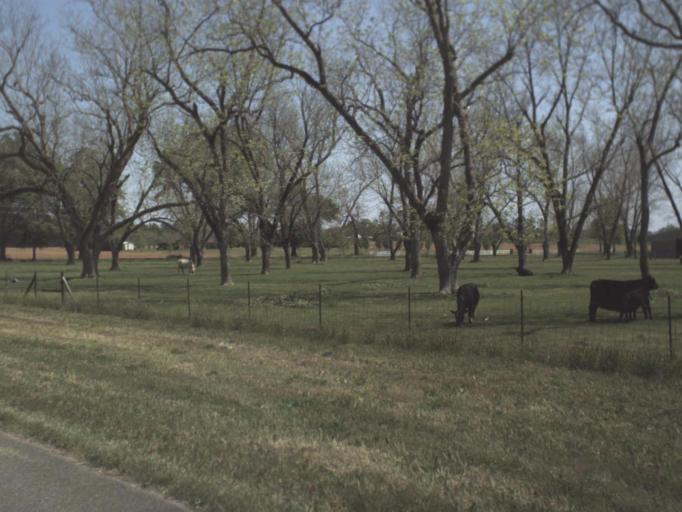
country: US
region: Alabama
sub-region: Escambia County
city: East Brewton
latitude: 30.8995
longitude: -87.0072
